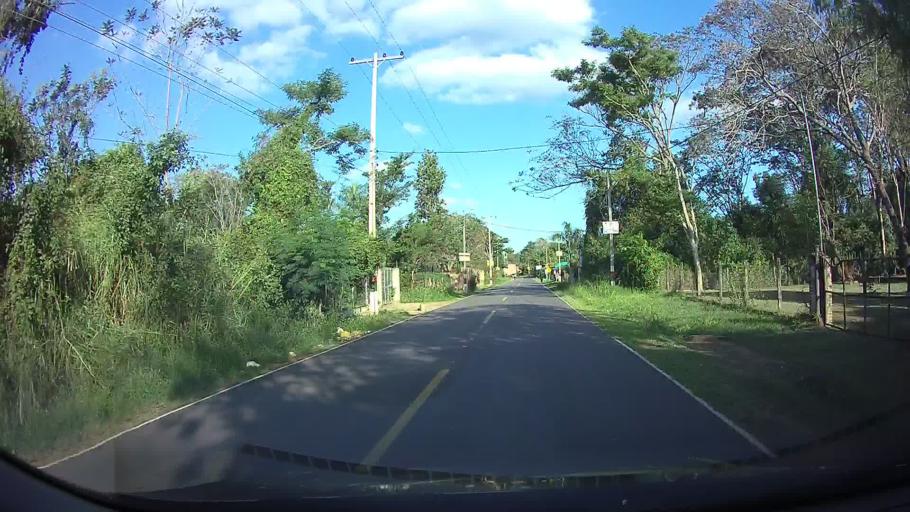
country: PY
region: Central
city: Aregua
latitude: -25.3019
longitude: -57.3895
